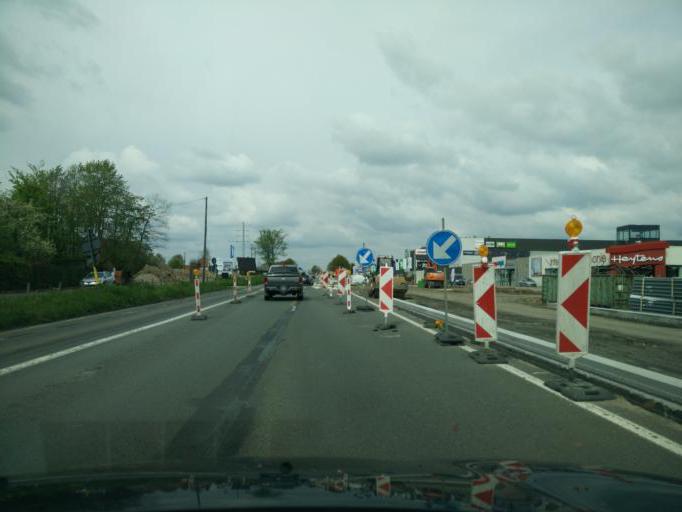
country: BE
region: Flanders
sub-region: Provincie Oost-Vlaanderen
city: Oudenaarde
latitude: 50.8710
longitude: 3.6086
